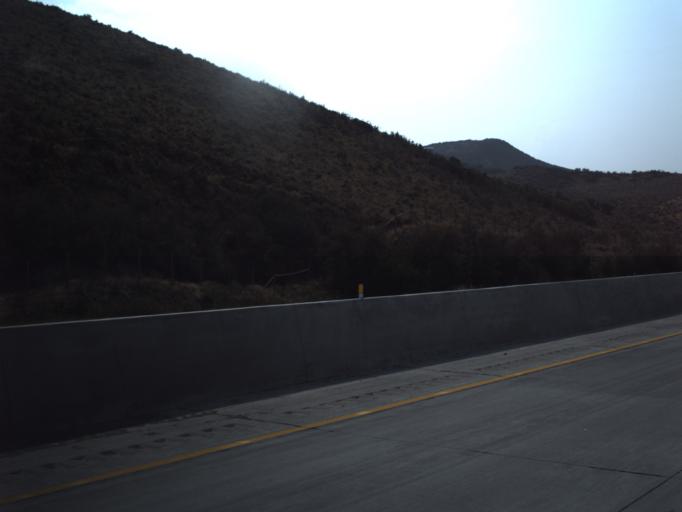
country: US
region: Utah
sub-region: Summit County
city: Coalville
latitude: 40.8079
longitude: -111.4214
